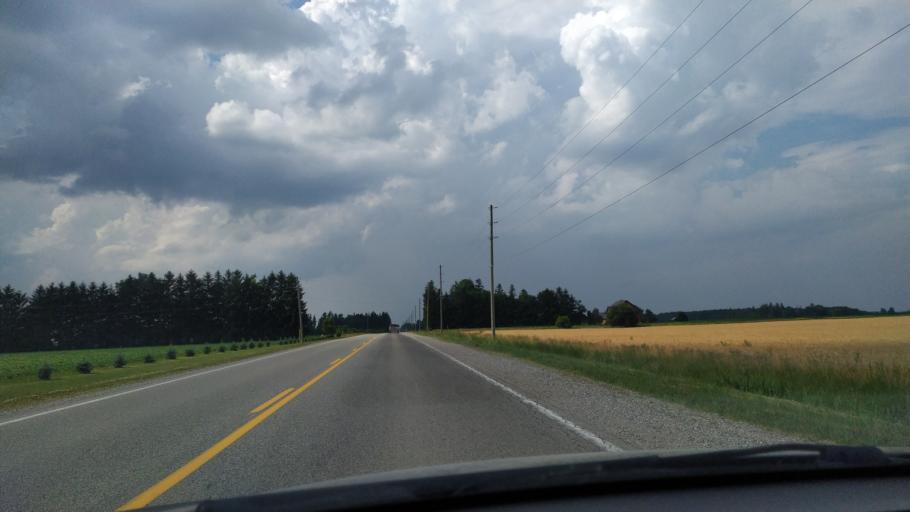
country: CA
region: Ontario
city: London
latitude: 43.1195
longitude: -81.1659
